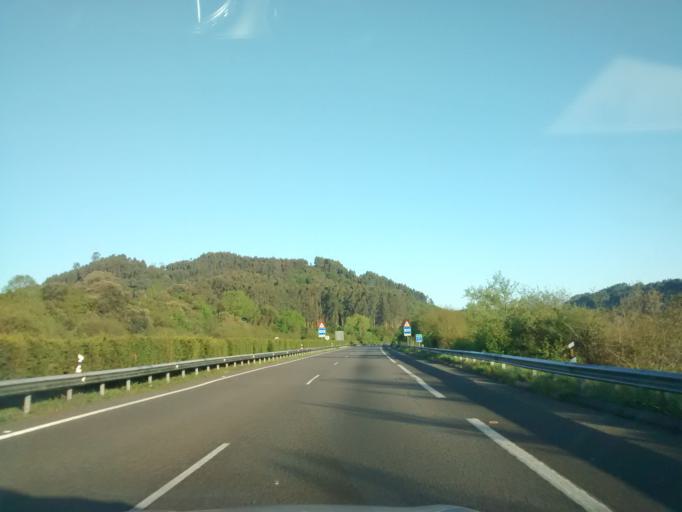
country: ES
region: Asturias
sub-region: Province of Asturias
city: Colunga
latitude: 43.4818
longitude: -5.3013
